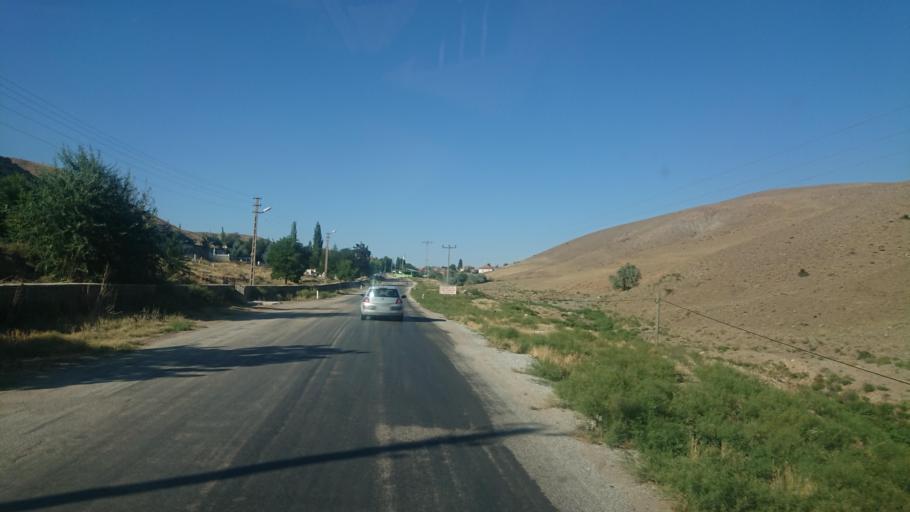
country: TR
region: Ankara
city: Sereflikochisar
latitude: 38.7587
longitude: 33.6957
